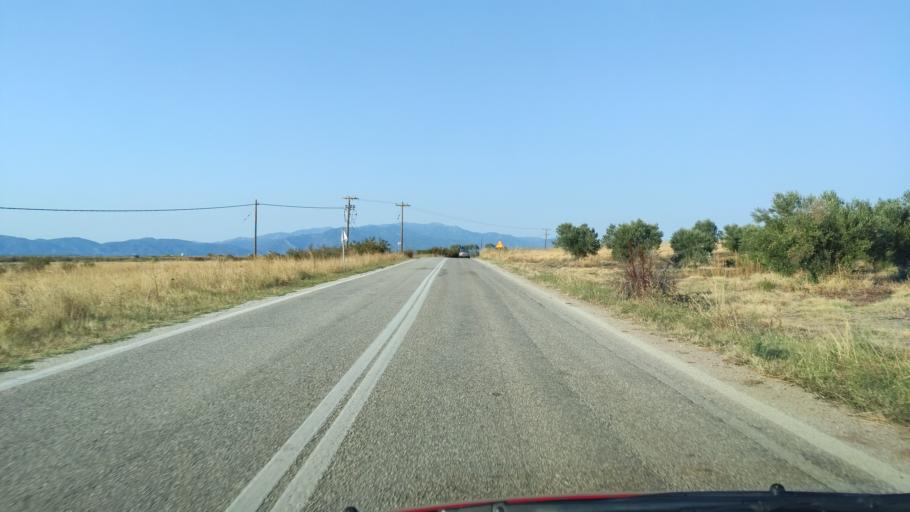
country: GR
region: East Macedonia and Thrace
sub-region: Nomos Rodopis
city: Iasmos
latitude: 40.9970
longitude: 25.1703
